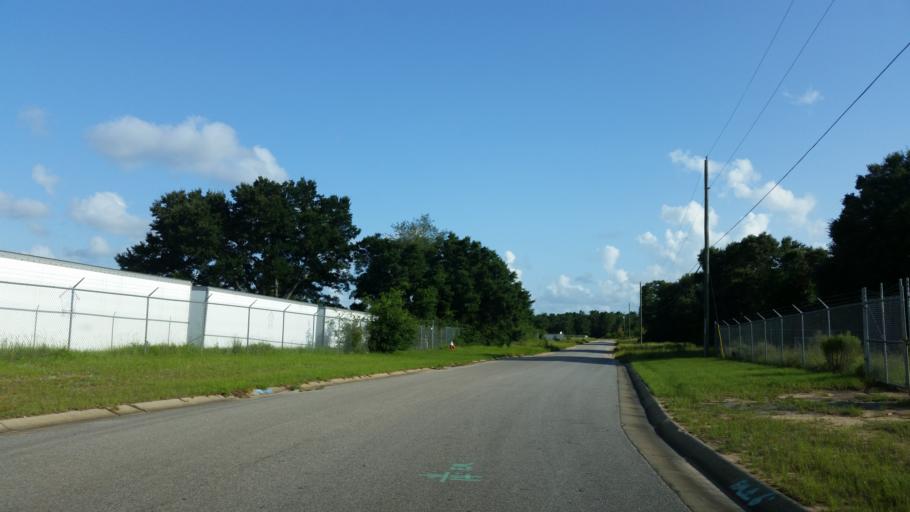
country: US
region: Florida
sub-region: Santa Rosa County
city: Bagdad
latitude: 30.5856
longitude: -87.0769
